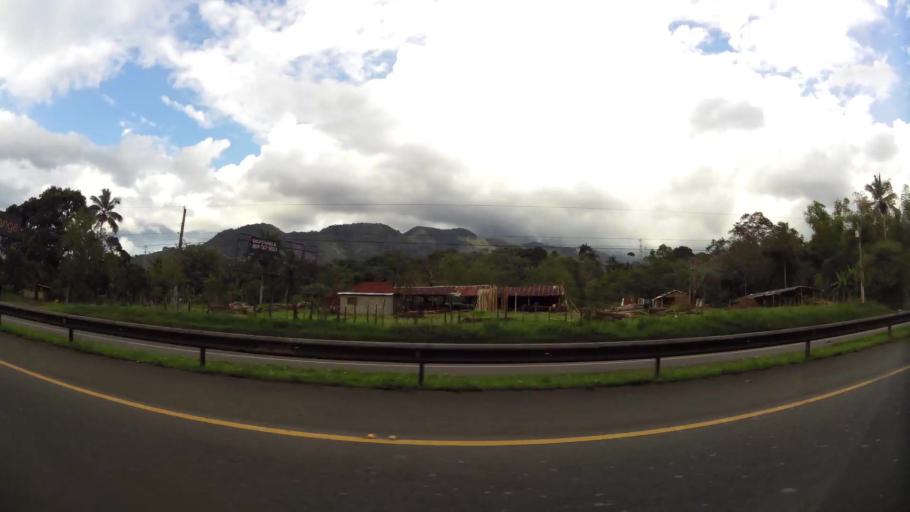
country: DO
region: Monsenor Nouel
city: Piedra Blanca
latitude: 18.8353
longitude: -70.3008
